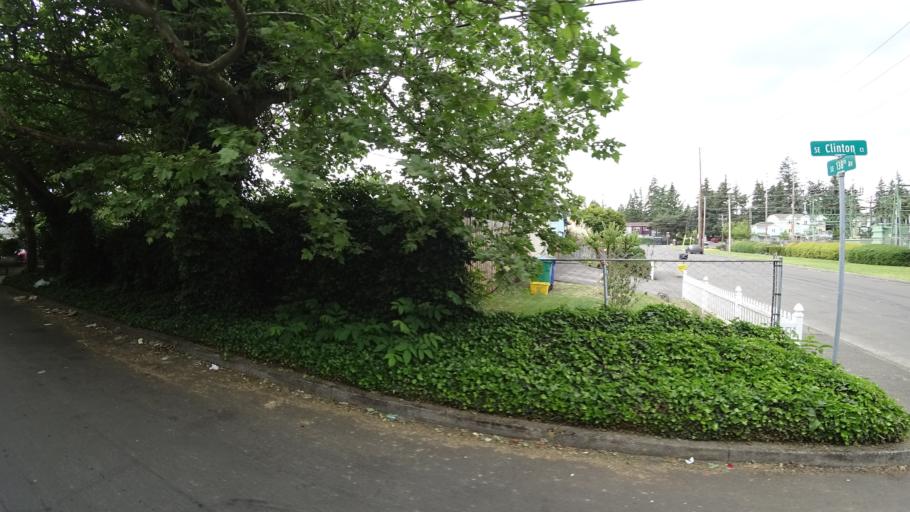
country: US
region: Oregon
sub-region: Multnomah County
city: Lents
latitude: 45.5031
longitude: -122.5215
